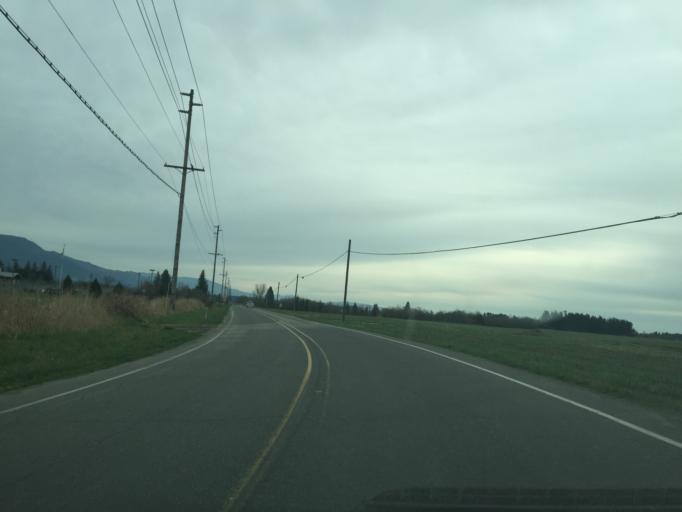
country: US
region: Washington
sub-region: Whatcom County
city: Sumas
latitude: 48.9923
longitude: -122.2858
